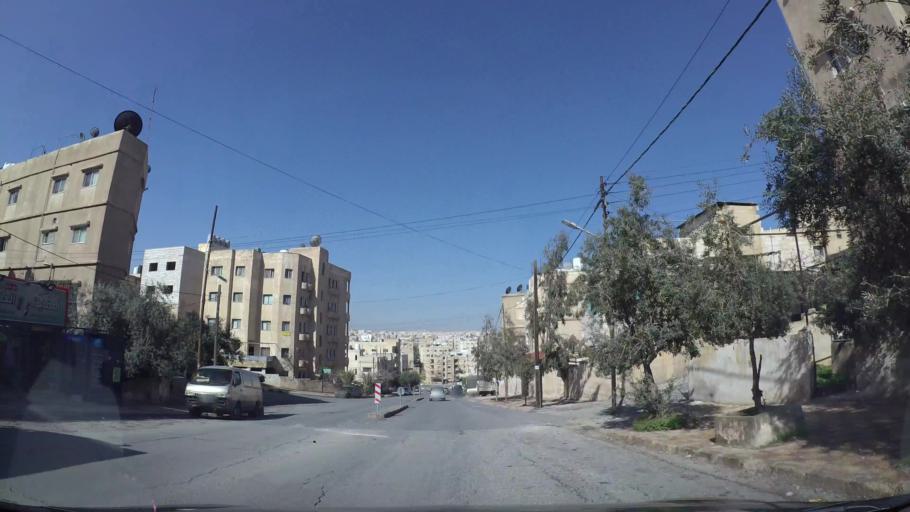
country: JO
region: Amman
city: Amman
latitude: 31.9859
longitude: 35.9858
